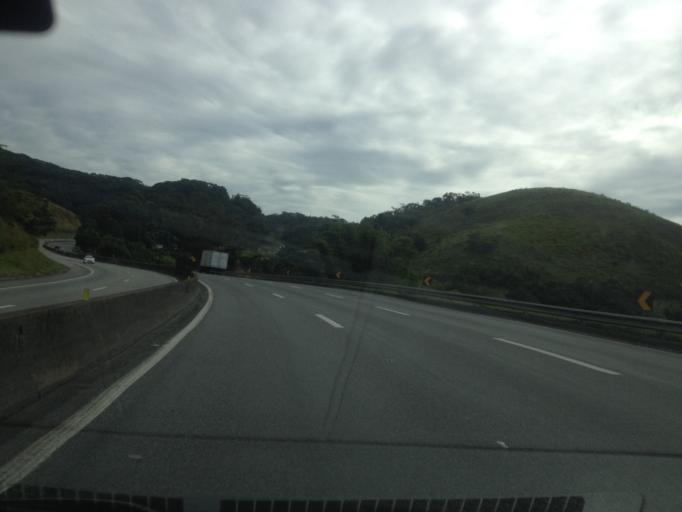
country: BR
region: Rio de Janeiro
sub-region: Pirai
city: Pirai
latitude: -22.6094
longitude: -43.9319
